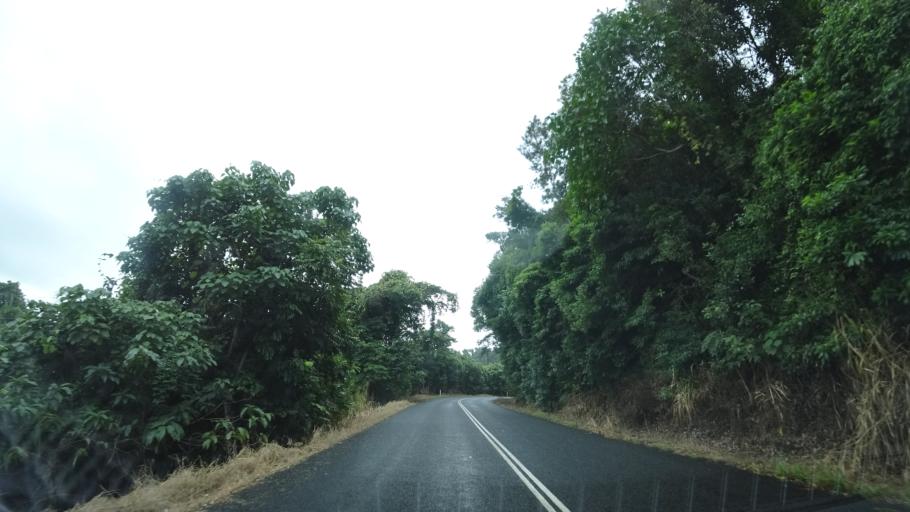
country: AU
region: Queensland
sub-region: Cassowary Coast
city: Innisfail
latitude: -17.5578
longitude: 146.0864
